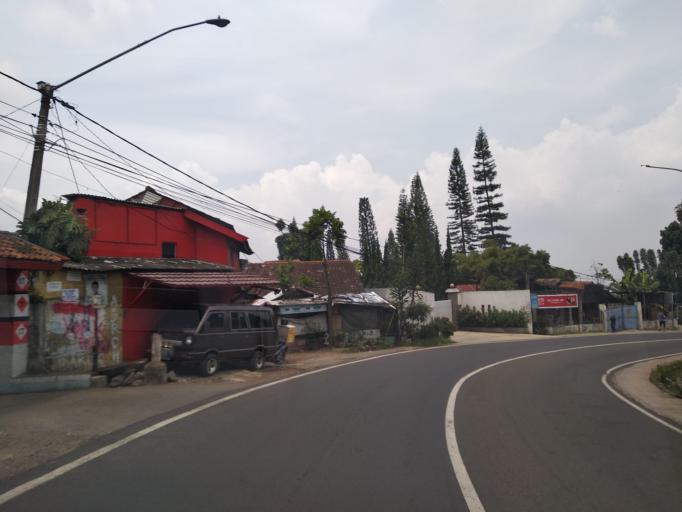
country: ID
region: West Java
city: Lembang
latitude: -6.8378
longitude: 107.5993
